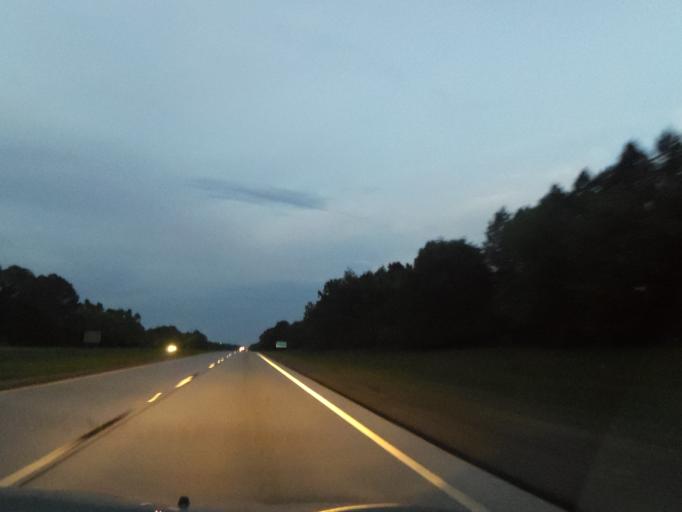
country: US
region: Georgia
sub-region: McDuffie County
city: Thomson
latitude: 33.5138
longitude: -82.4730
